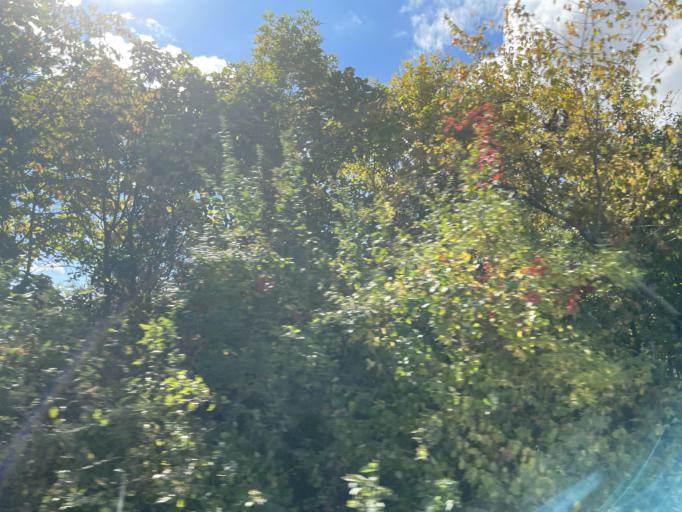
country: US
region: Indiana
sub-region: Allen County
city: Fort Wayne
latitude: 41.1183
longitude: -85.2384
